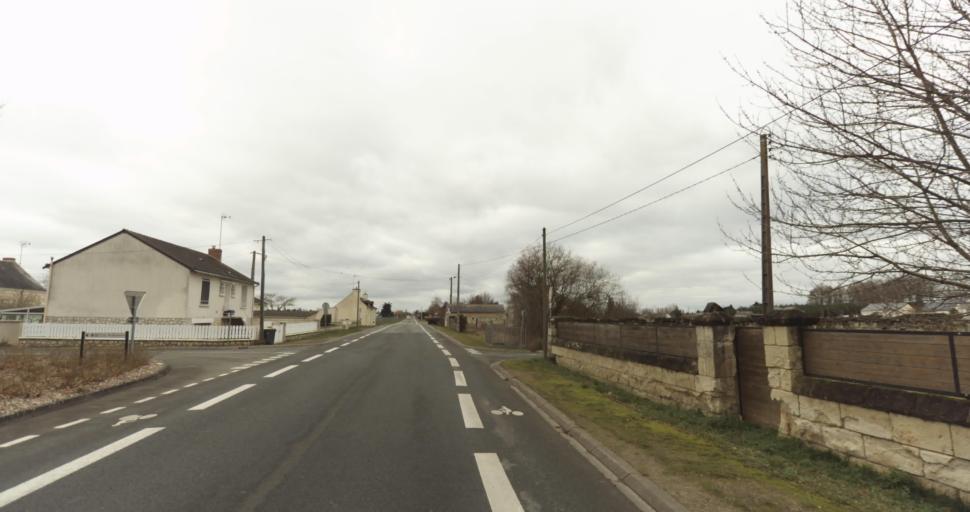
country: FR
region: Pays de la Loire
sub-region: Departement de Maine-et-Loire
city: Allonnes
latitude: 47.2953
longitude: 0.0138
